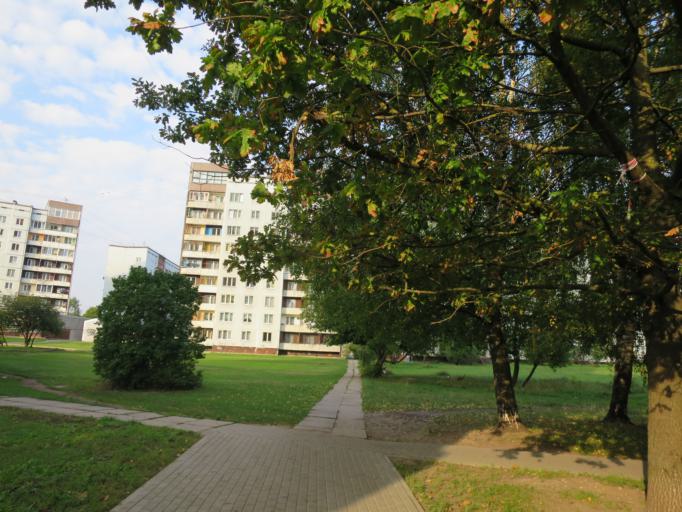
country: LV
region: Stopini
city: Ulbroka
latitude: 56.9670
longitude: 24.2370
